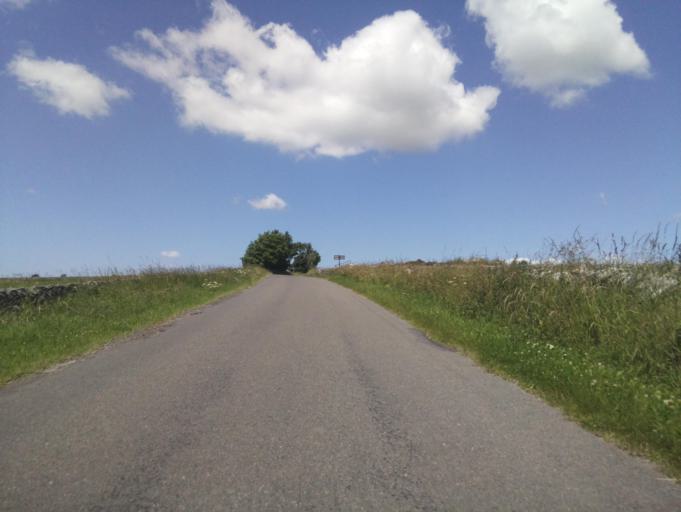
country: GB
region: England
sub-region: Derbyshire
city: Tideswell
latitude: 53.2252
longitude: -1.7830
